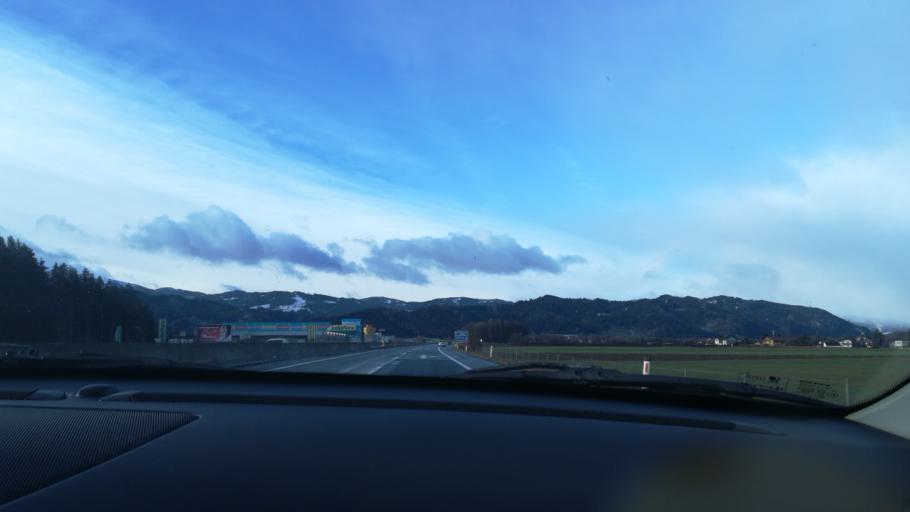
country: AT
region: Styria
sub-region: Politischer Bezirk Murtal
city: Fohnsdorf
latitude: 47.1864
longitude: 14.6922
